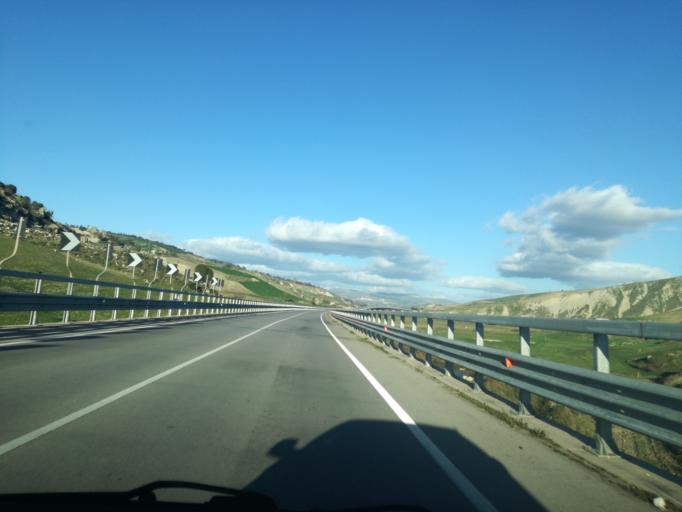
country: IT
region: Sicily
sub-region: Enna
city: Pietraperzia
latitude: 37.4241
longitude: 14.0737
